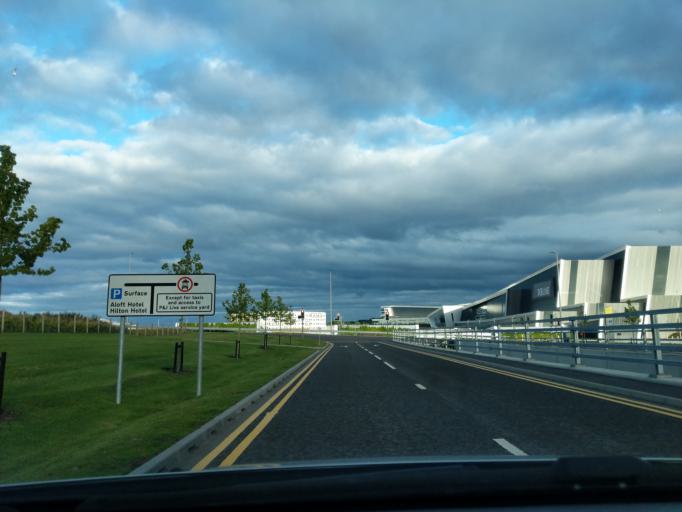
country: GB
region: Scotland
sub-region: Aberdeen City
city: Dyce
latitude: 57.1879
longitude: -2.1950
